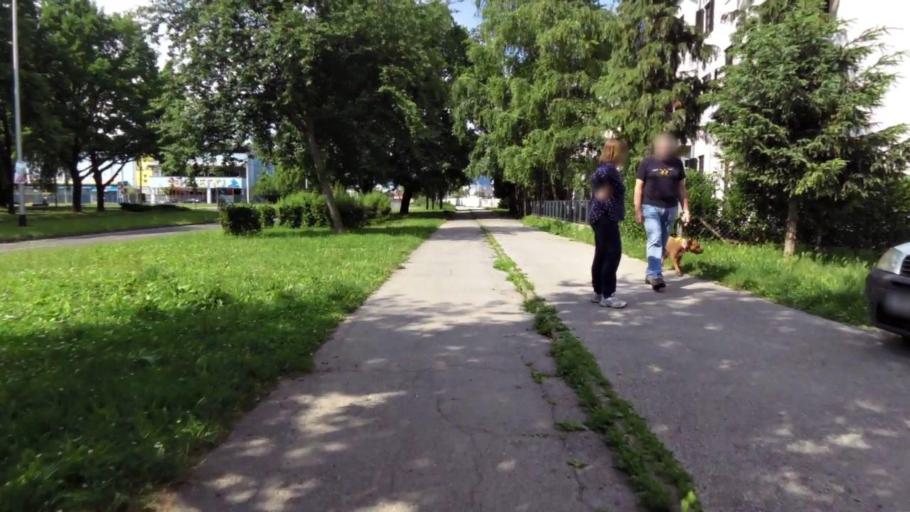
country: HR
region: Grad Zagreb
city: Jankomir
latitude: 45.7930
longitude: 15.9226
